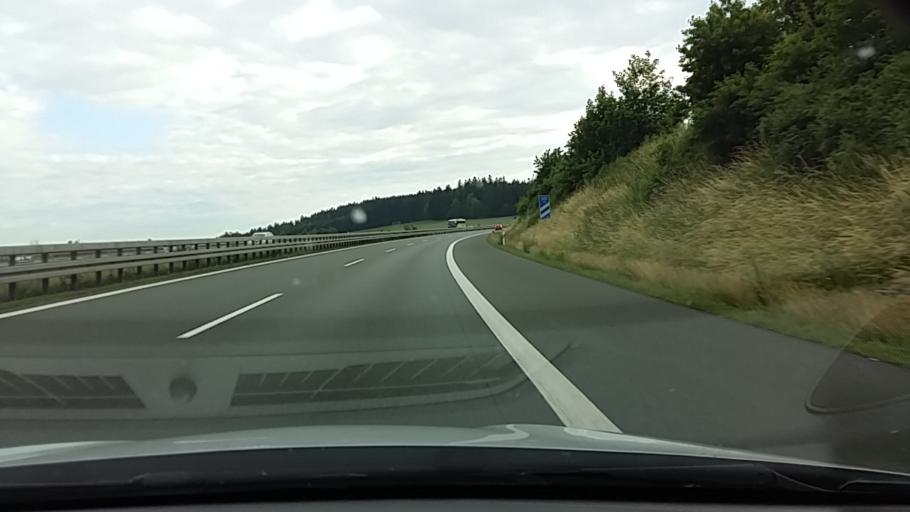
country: DE
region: Bavaria
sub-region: Upper Palatinate
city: Leuchtenberg
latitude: 49.5791
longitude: 12.2762
